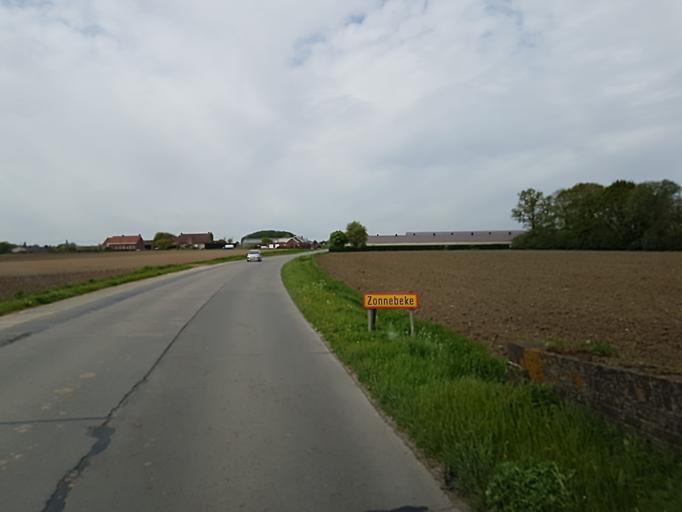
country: BE
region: Flanders
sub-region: Provincie West-Vlaanderen
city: Zonnebeke
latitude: 50.8775
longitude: 3.0251
